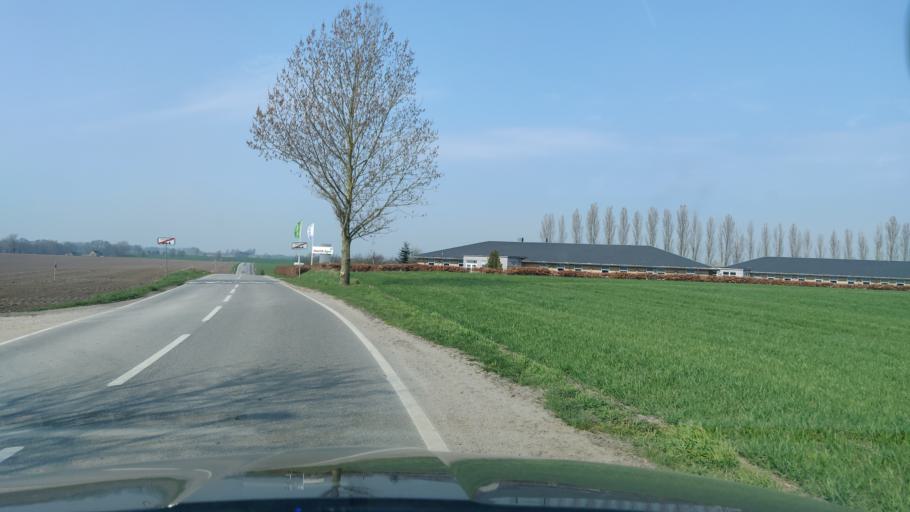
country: DK
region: South Denmark
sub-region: Nordfyns Kommune
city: Sonderso
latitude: 55.5155
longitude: 10.2699
